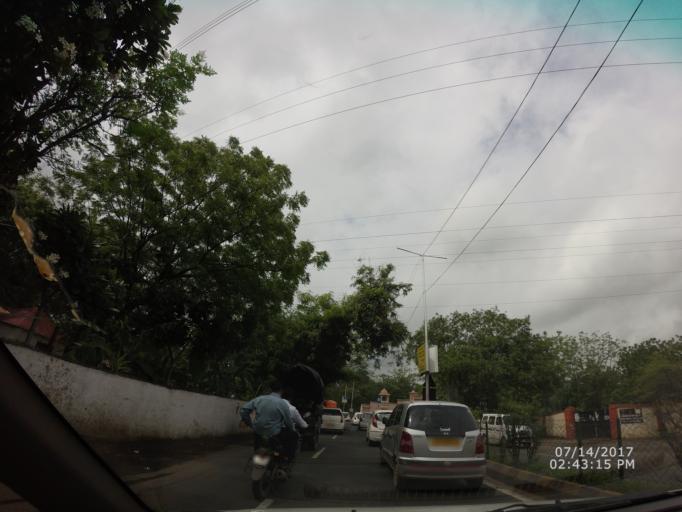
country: IN
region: Gujarat
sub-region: Ahmadabad
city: Ahmedabad
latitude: 23.0654
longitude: 72.6001
